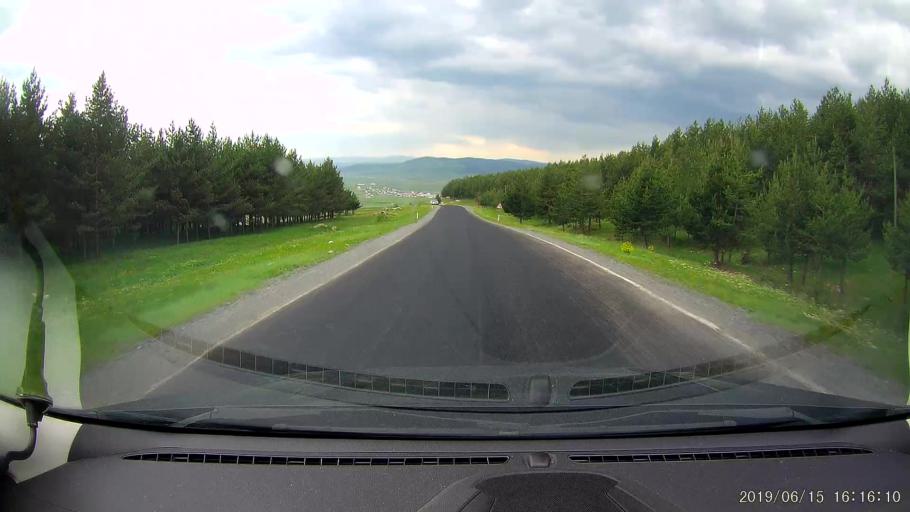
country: TR
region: Ardahan
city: Hanak
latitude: 41.2616
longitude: 42.8528
